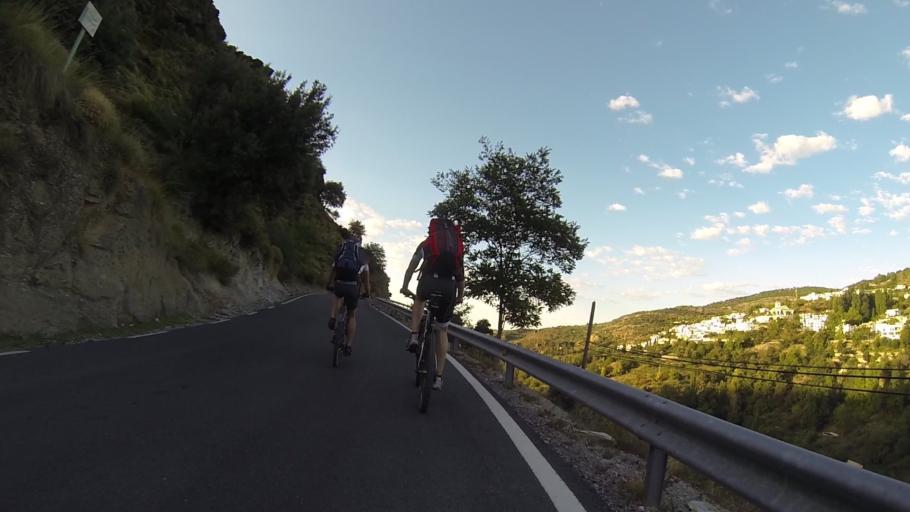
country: ES
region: Andalusia
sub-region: Provincia de Granada
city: Berchules
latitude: 36.9856
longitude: -3.1495
